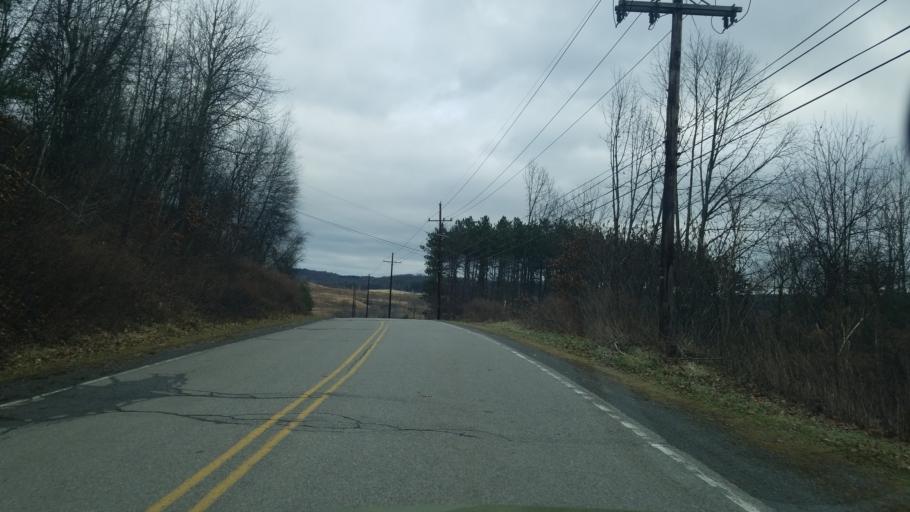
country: US
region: Pennsylvania
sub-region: Clearfield County
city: Clearfield
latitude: 41.0284
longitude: -78.4021
